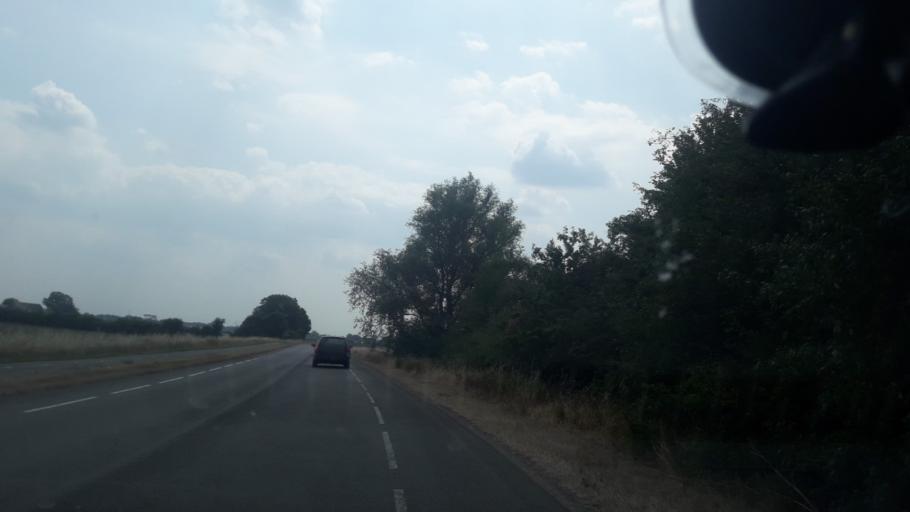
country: NL
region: Gelderland
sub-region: Gemeente Rheden
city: Ellecom
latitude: 52.0342
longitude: 6.1065
